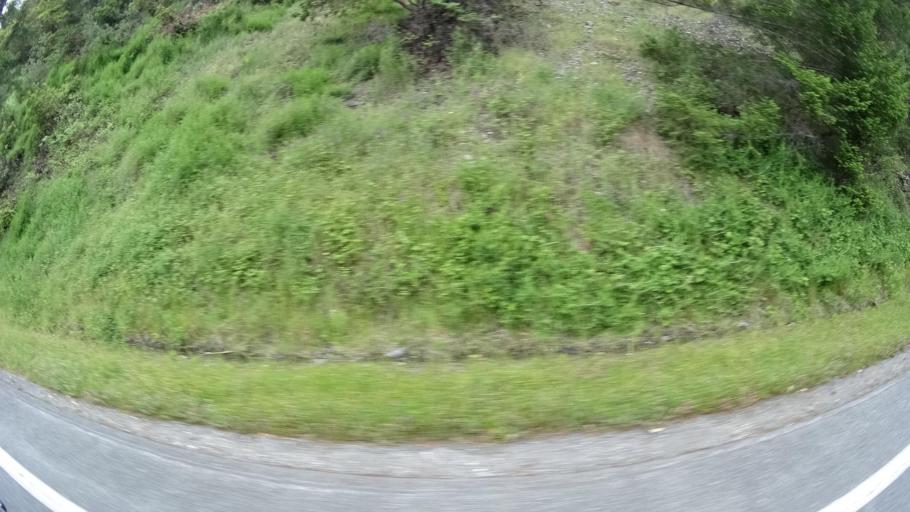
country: US
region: California
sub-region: Humboldt County
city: Willow Creek
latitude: 41.2821
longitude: -123.5819
